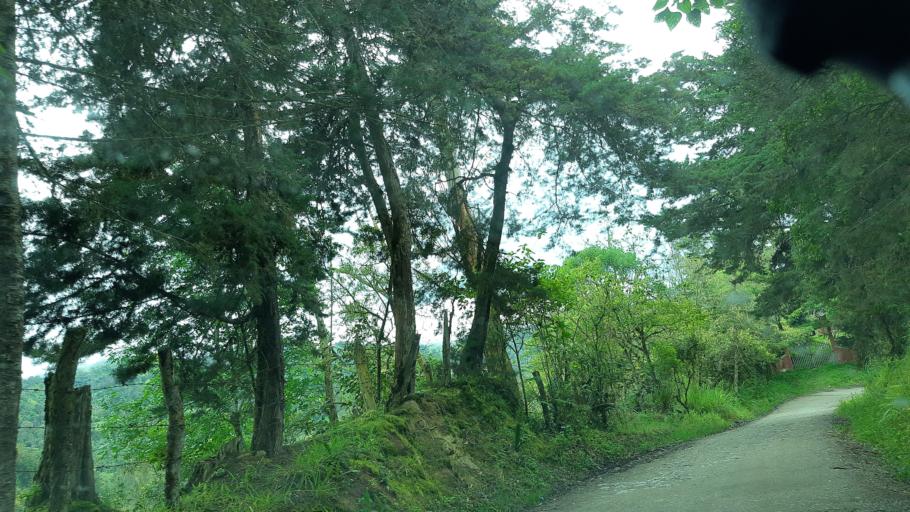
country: CO
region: Boyaca
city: Garagoa
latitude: 5.0705
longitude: -73.3557
